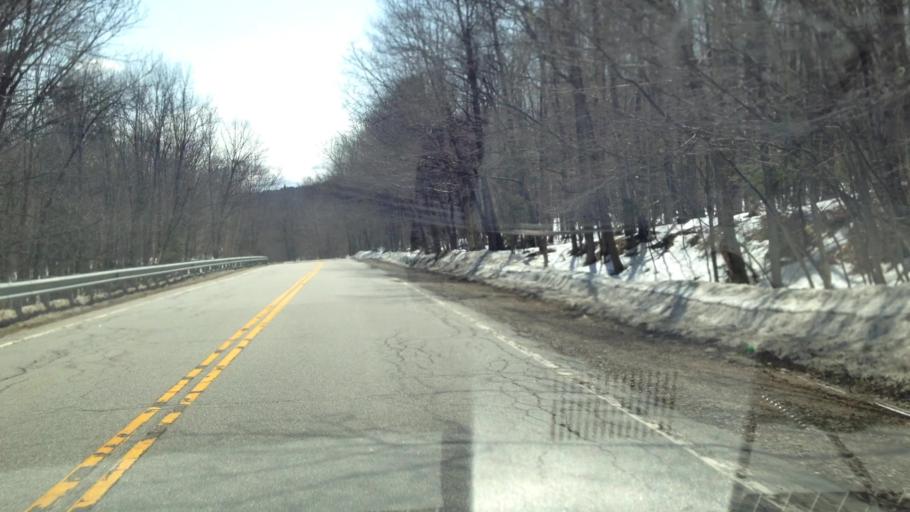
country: US
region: New Hampshire
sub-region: Sullivan County
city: Springfield
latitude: 43.4877
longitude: -71.9791
